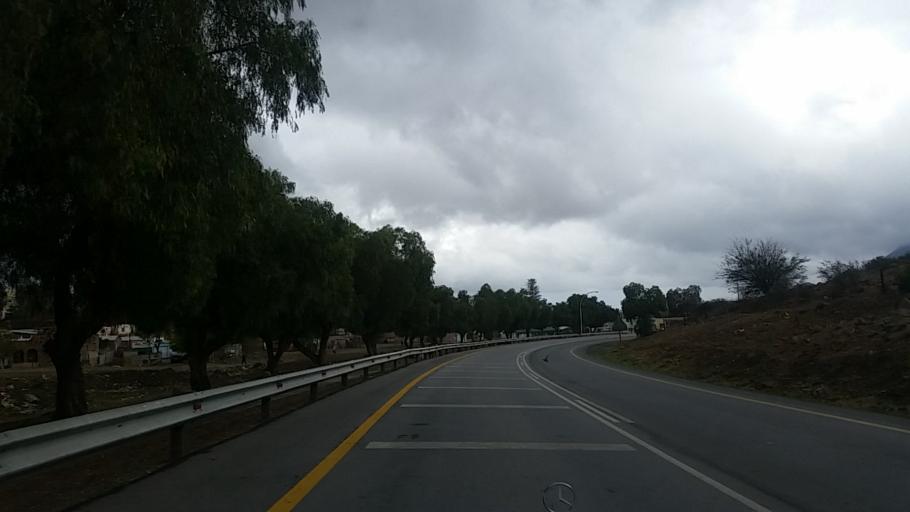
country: ZA
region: Eastern Cape
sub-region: Cacadu District Municipality
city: Graaff-Reinet
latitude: -32.2443
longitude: 24.5379
